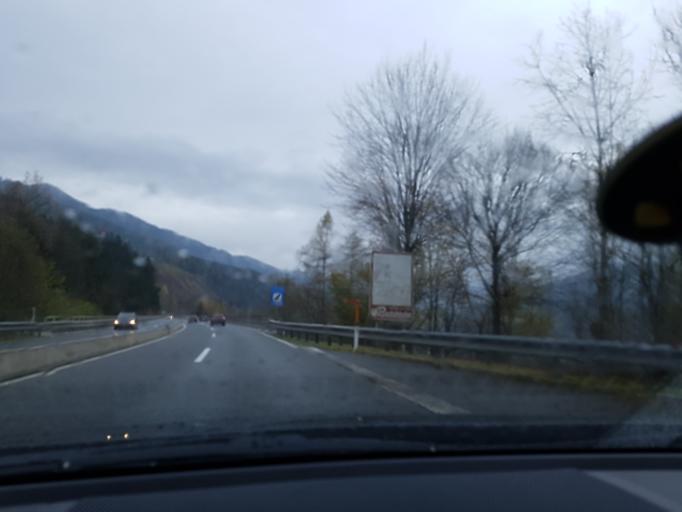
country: AT
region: Salzburg
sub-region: Politischer Bezirk Sankt Johann im Pongau
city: Bischofshofen
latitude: 47.4279
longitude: 13.2243
